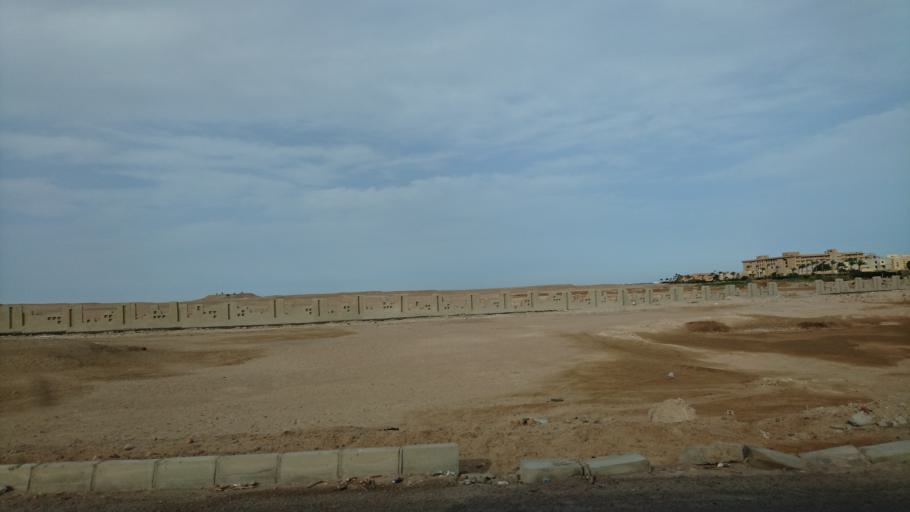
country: EG
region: Red Sea
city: Bur Safajah
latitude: 26.8016
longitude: 33.9384
